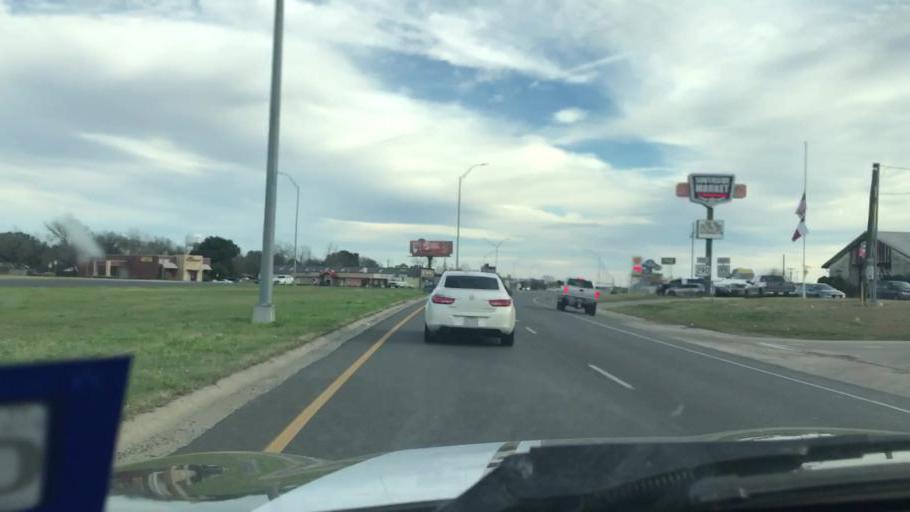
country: US
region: Texas
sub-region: Bastrop County
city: Elgin
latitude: 30.3506
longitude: -97.3864
